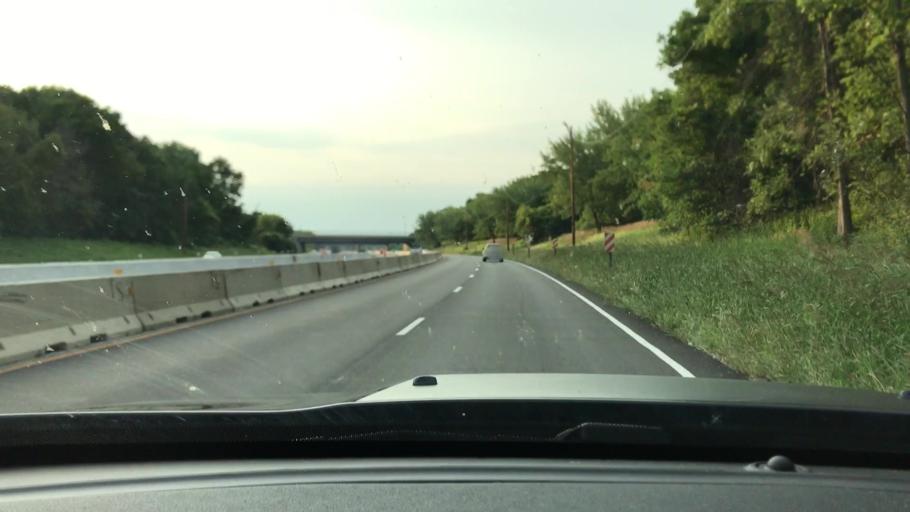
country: US
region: Illinois
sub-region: Rock Island County
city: Moline
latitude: 41.4819
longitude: -90.4954
